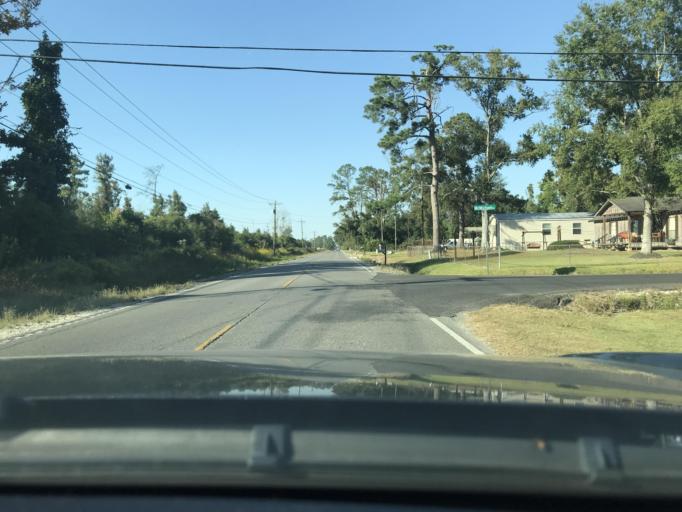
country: US
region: Louisiana
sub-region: Calcasieu Parish
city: Moss Bluff
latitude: 30.3176
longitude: -93.2583
